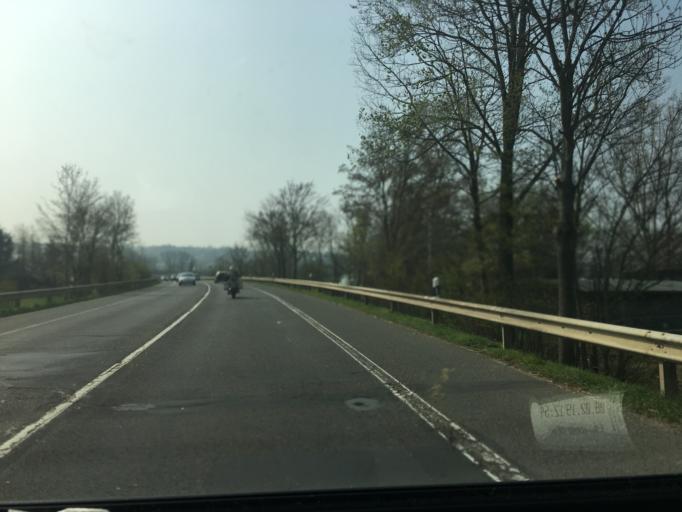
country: DE
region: North Rhine-Westphalia
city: Bornheim
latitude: 50.7687
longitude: 6.9757
